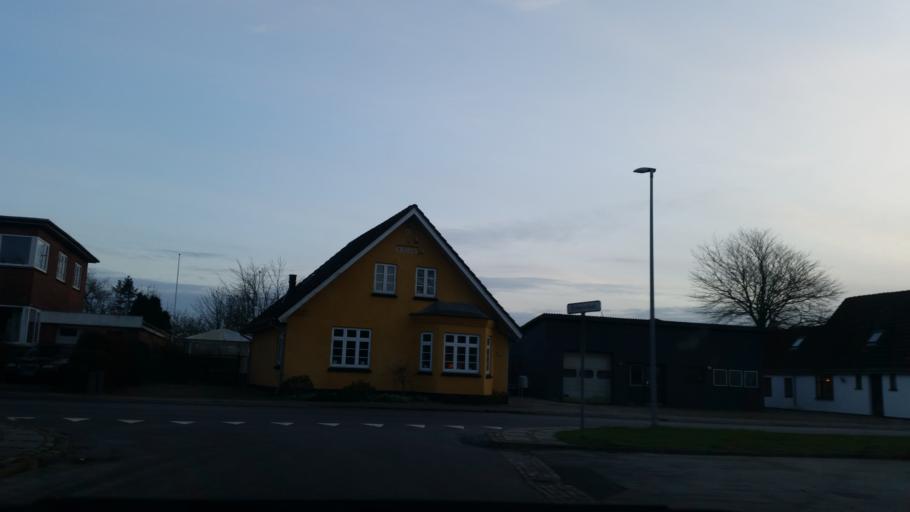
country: DK
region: South Denmark
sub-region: Vejen Kommune
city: Brorup
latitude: 55.4090
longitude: 8.9756
